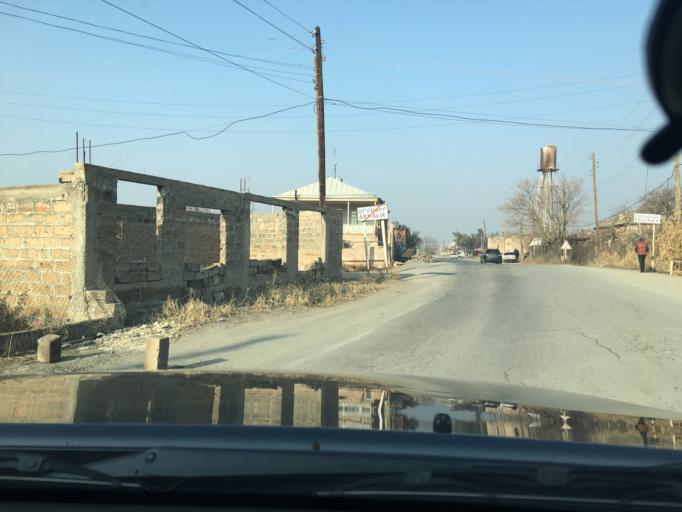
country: AM
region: Armavir
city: Aygeshat
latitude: 40.0876
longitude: 44.0475
